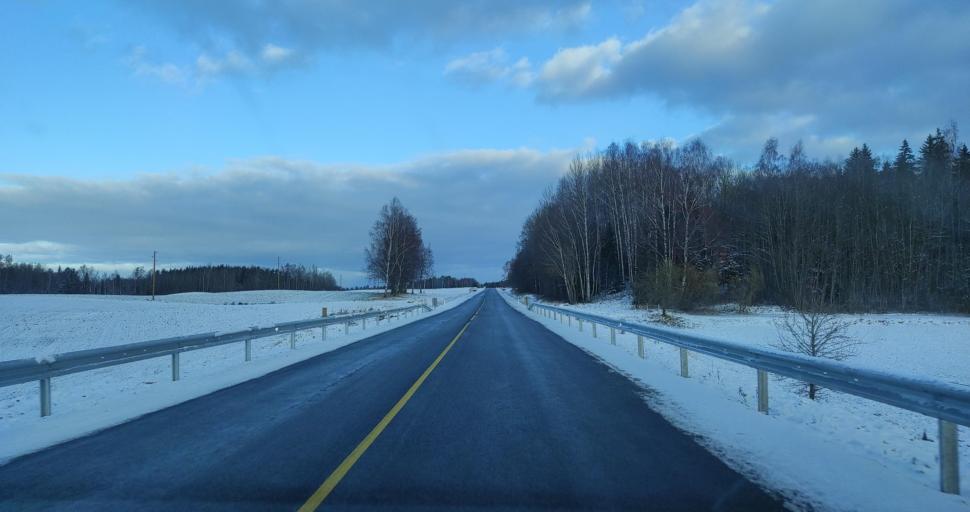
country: LV
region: Skrunda
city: Skrunda
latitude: 56.7151
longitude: 22.0109
